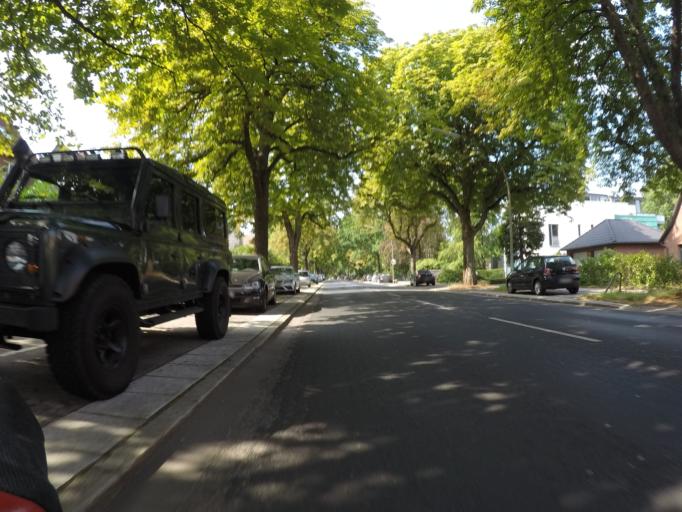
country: DE
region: Hamburg
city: Hummelsbuettel
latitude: 53.6342
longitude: 10.0492
